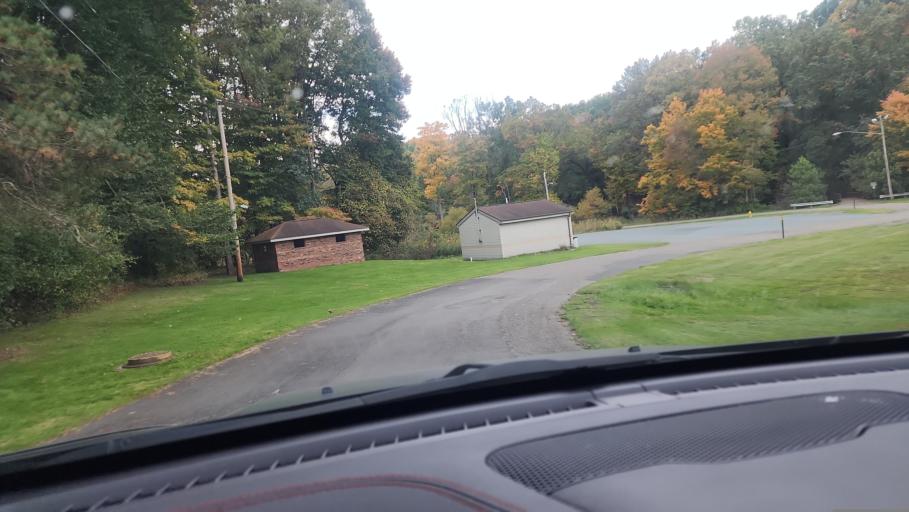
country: US
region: Ohio
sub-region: Trumbull County
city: Churchill
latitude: 41.1592
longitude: -80.6684
